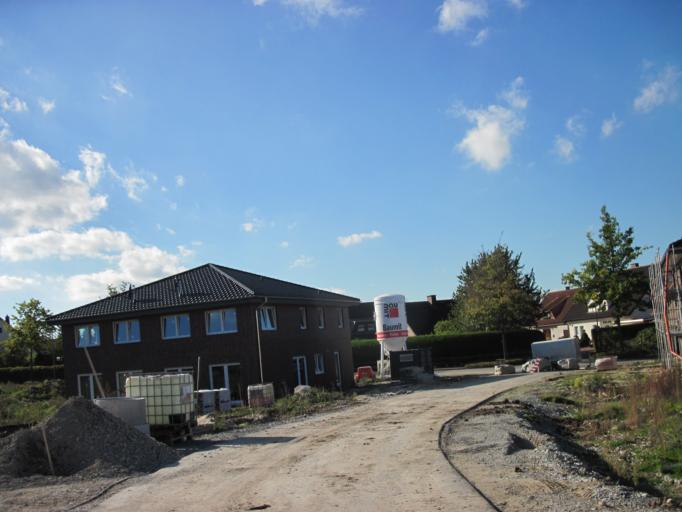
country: DE
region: North Rhine-Westphalia
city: Geseke
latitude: 51.6312
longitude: 8.5048
